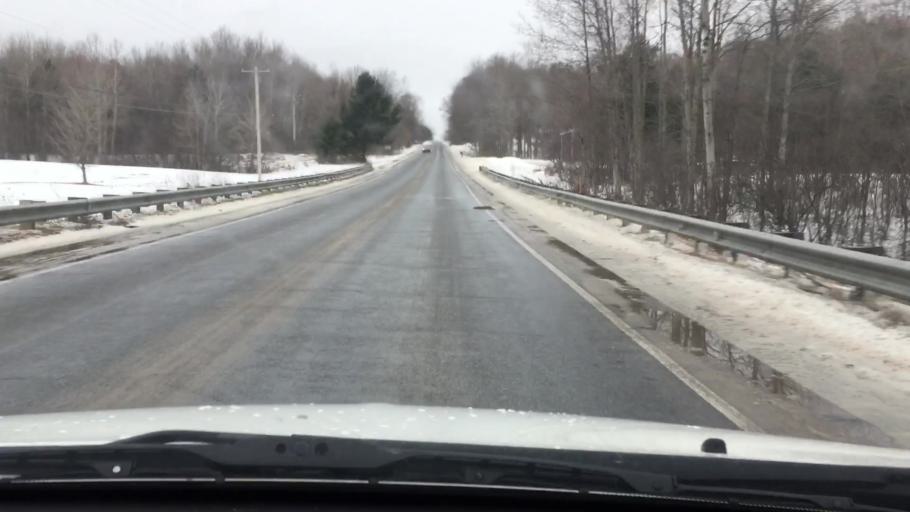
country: US
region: Michigan
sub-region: Wexford County
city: Cadillac
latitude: 44.1018
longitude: -85.4443
